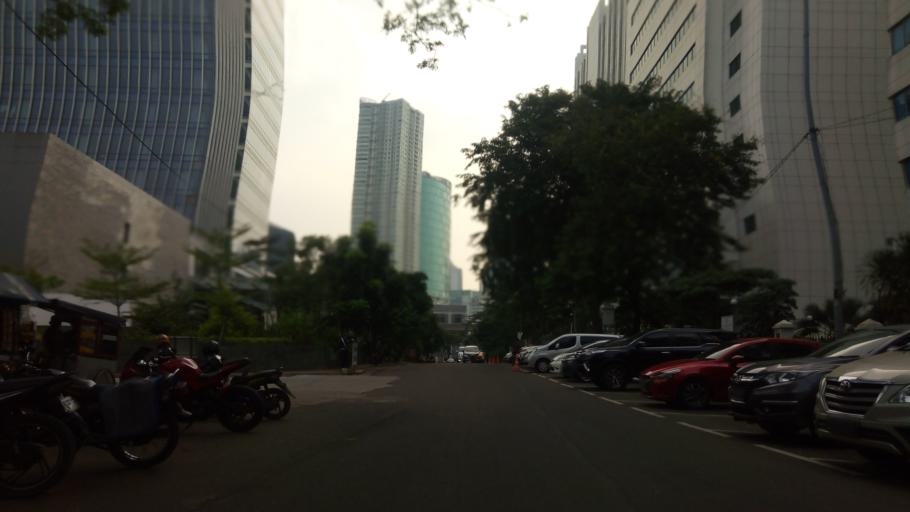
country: ID
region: Jakarta Raya
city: Jakarta
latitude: -6.2233
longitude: 106.8346
